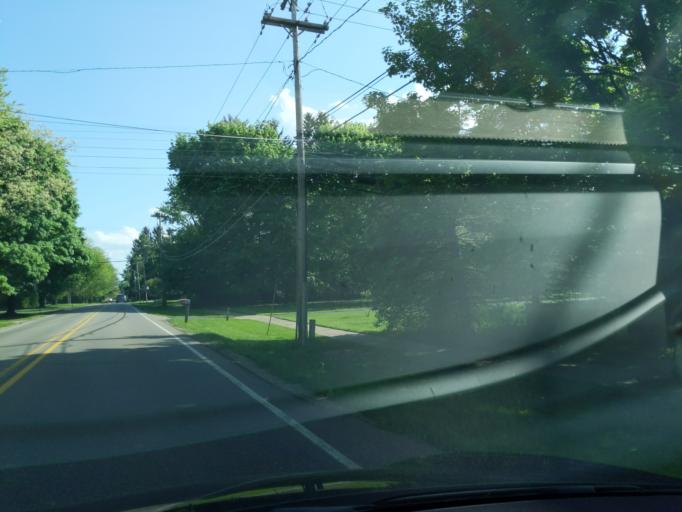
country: US
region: Michigan
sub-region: Ingham County
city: Okemos
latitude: 42.7122
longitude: -84.4104
